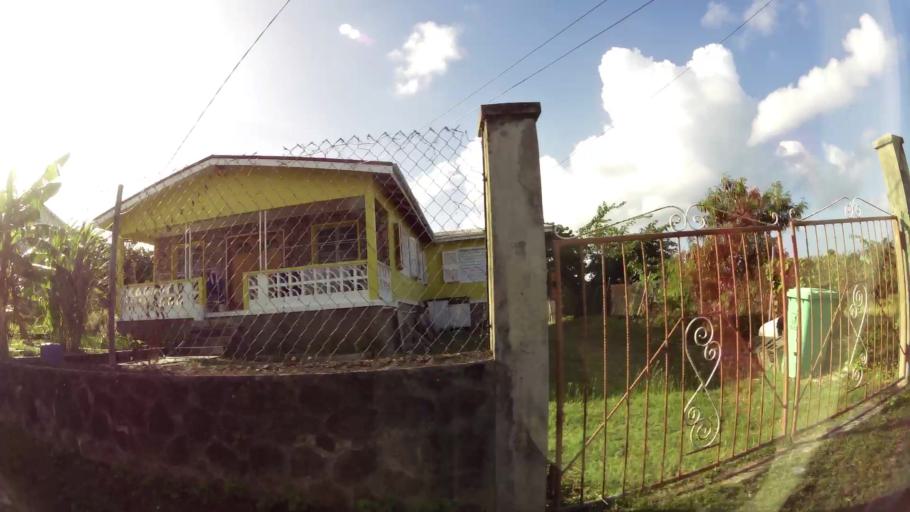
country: KN
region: Saint Paul Charlestown
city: Charlestown
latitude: 17.1396
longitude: -62.6247
